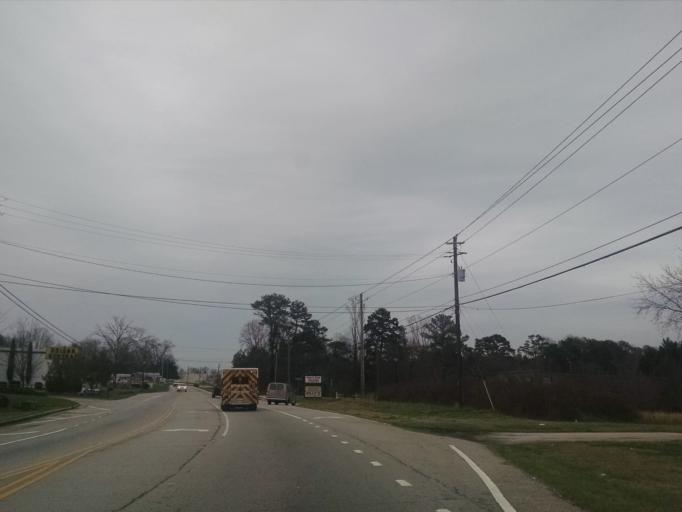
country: US
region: Georgia
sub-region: Hall County
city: Oakwood
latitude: 34.2156
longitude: -83.8717
